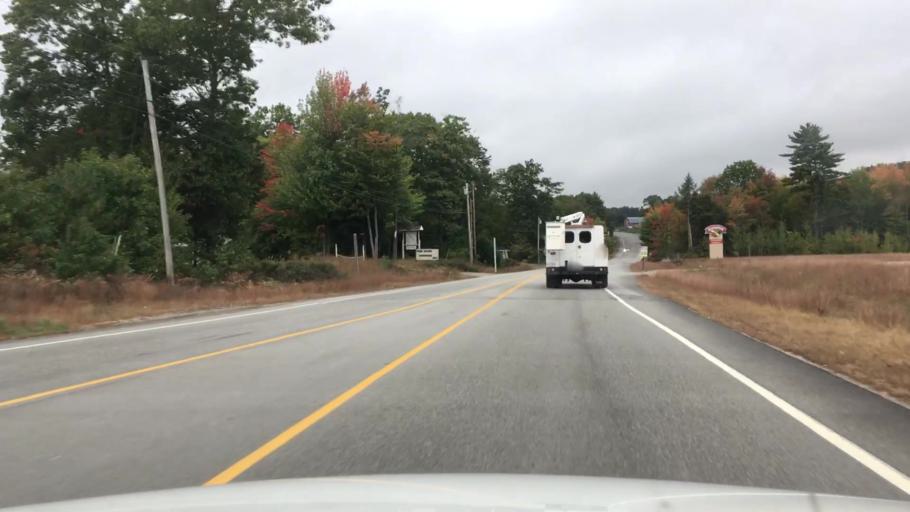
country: US
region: Maine
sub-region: Androscoggin County
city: Poland
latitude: 44.0766
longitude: -70.4170
